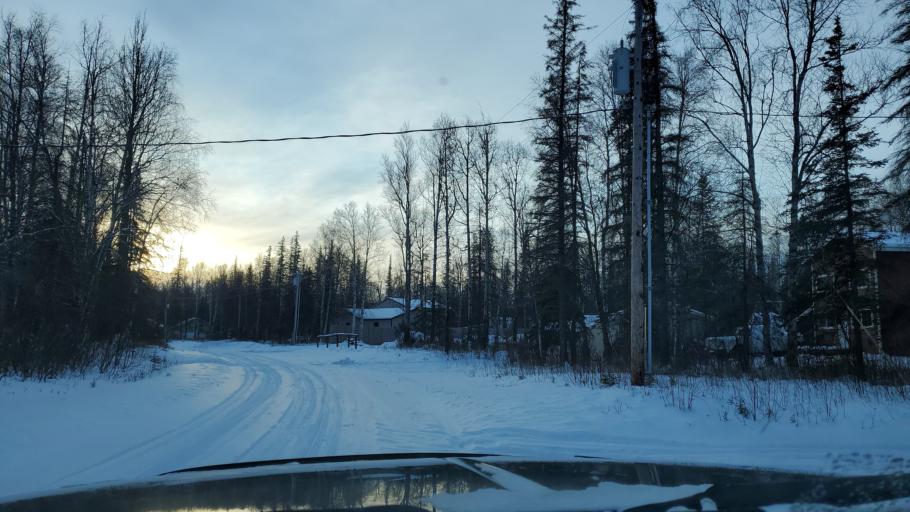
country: US
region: Alaska
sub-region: Matanuska-Susitna Borough
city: Lakes
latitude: 61.6667
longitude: -149.2971
